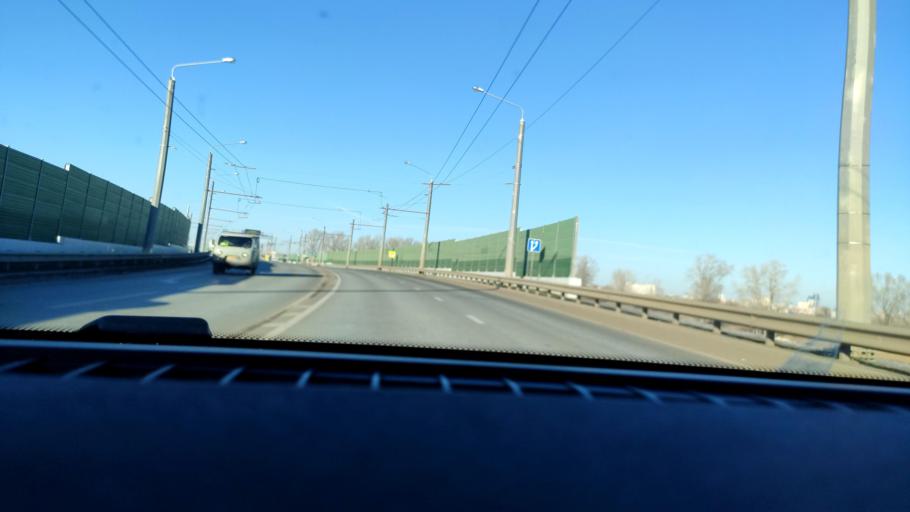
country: RU
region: Samara
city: Samara
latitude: 53.1585
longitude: 50.0918
